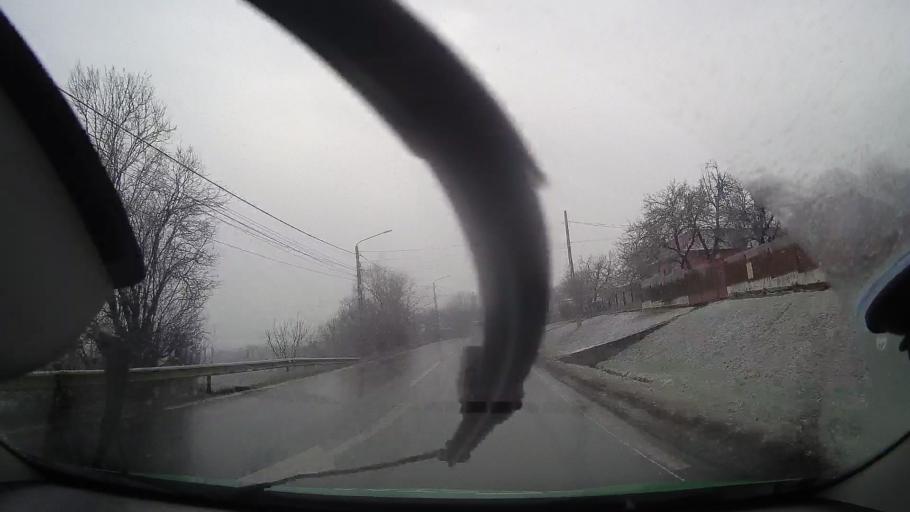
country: RO
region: Mures
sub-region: Comuna Bagaciu
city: Delenii
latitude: 46.2722
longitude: 24.3007
